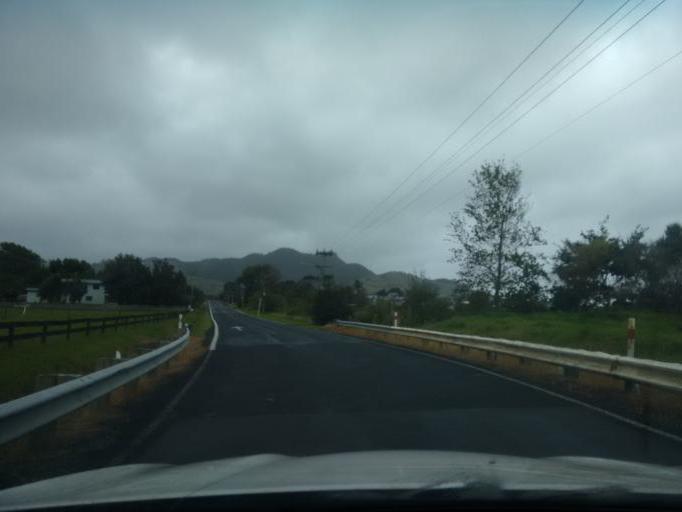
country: NZ
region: Waikato
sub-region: Thames-Coromandel District
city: Whitianga
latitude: -36.8021
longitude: 175.7191
